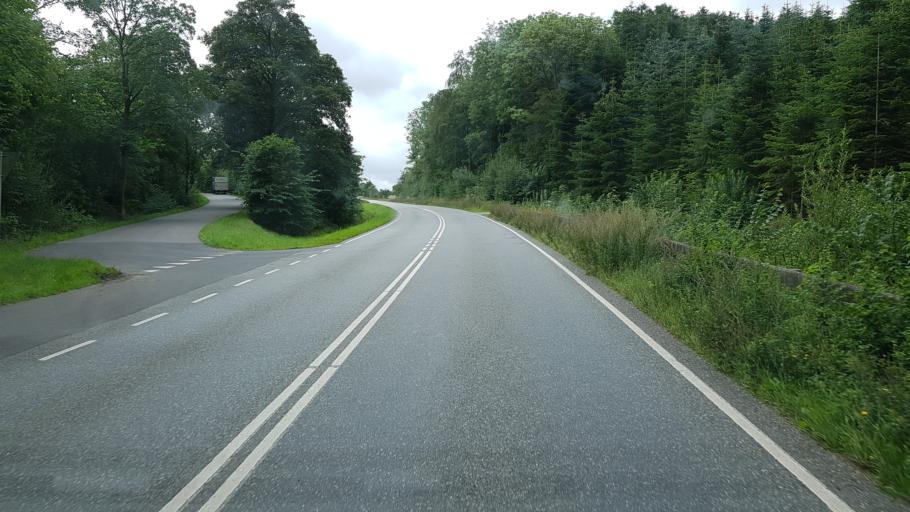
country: DK
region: South Denmark
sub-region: Kolding Kommune
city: Kolding
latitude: 55.4799
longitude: 9.4101
